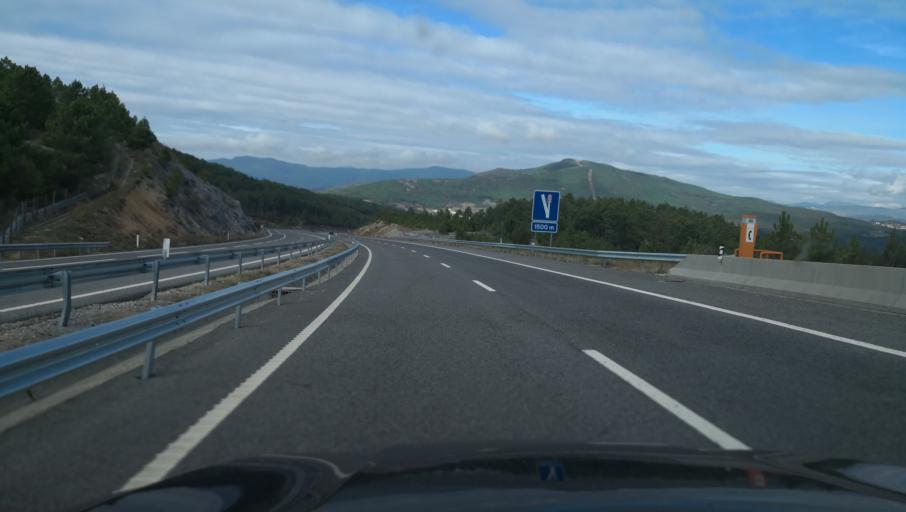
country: PT
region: Vila Real
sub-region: Vila Pouca de Aguiar
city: Vila Pouca de Aguiar
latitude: 41.5603
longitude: -7.6274
